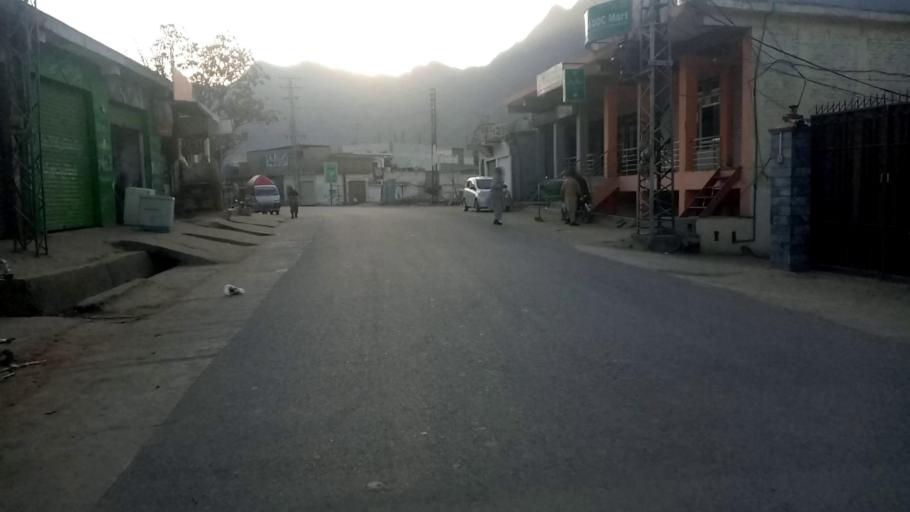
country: PK
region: Khyber Pakhtunkhwa
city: Saidu Sharif
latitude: 34.7408
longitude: 72.3418
